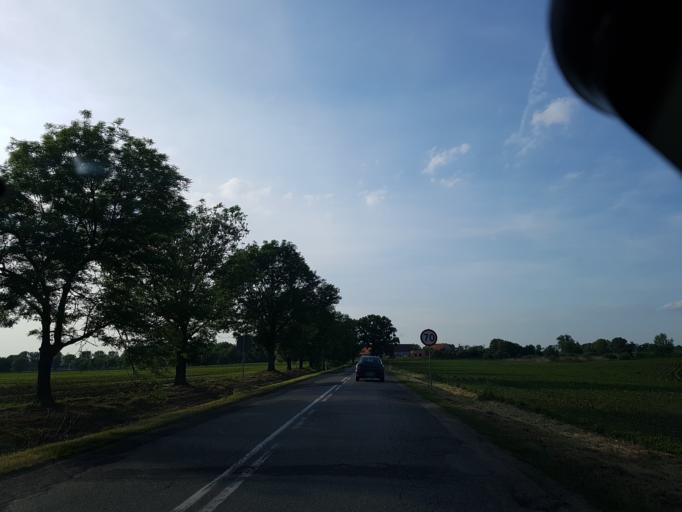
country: PL
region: Lower Silesian Voivodeship
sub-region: Powiat wroclawski
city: Kobierzyce
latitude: 50.9452
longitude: 16.9209
